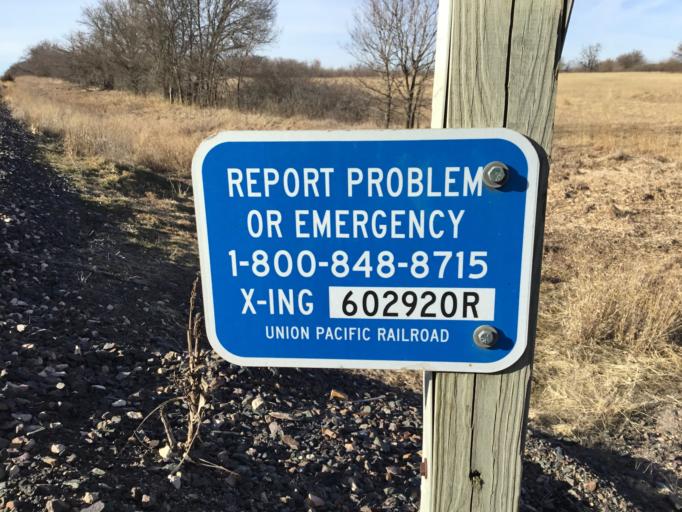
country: US
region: Kansas
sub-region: Marion County
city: Hillsboro
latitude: 38.4036
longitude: -97.4090
